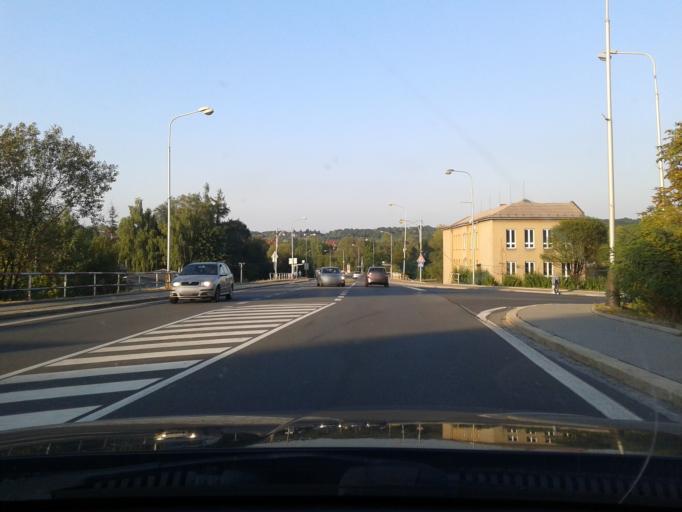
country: CZ
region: Moravskoslezsky
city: Orlova
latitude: 49.8524
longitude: 18.4210
